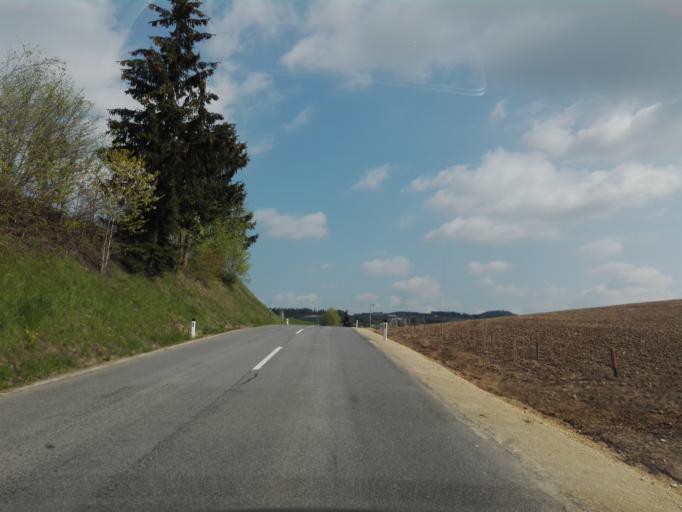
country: AT
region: Upper Austria
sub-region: Politischer Bezirk Perg
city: Perg
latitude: 48.2716
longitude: 14.6540
